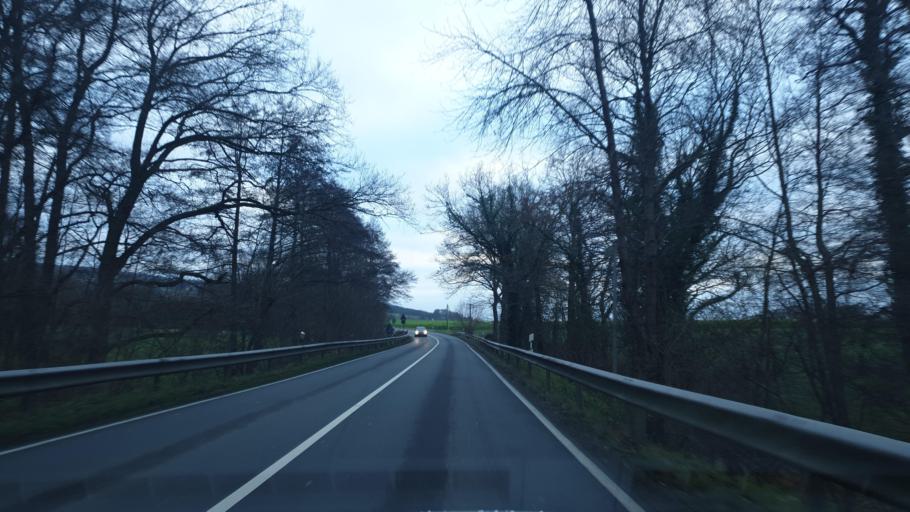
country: DE
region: North Rhine-Westphalia
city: Loehne
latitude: 52.1675
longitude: 8.6831
